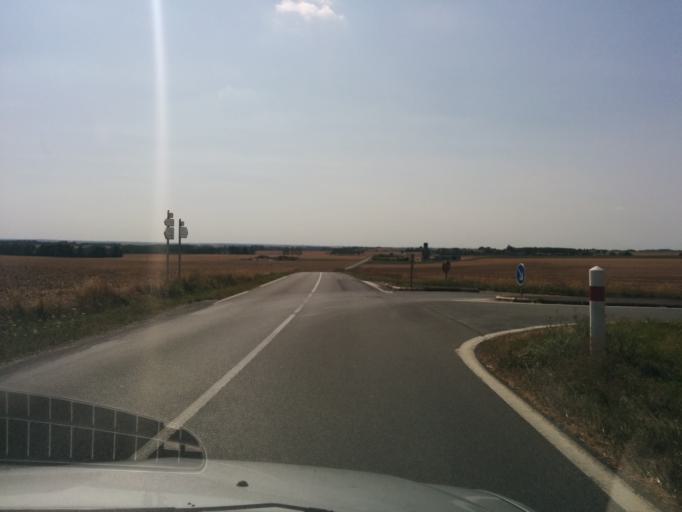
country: FR
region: Poitou-Charentes
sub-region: Departement de la Vienne
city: Saint-Jean-de-Sauves
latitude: 46.8000
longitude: 0.0998
